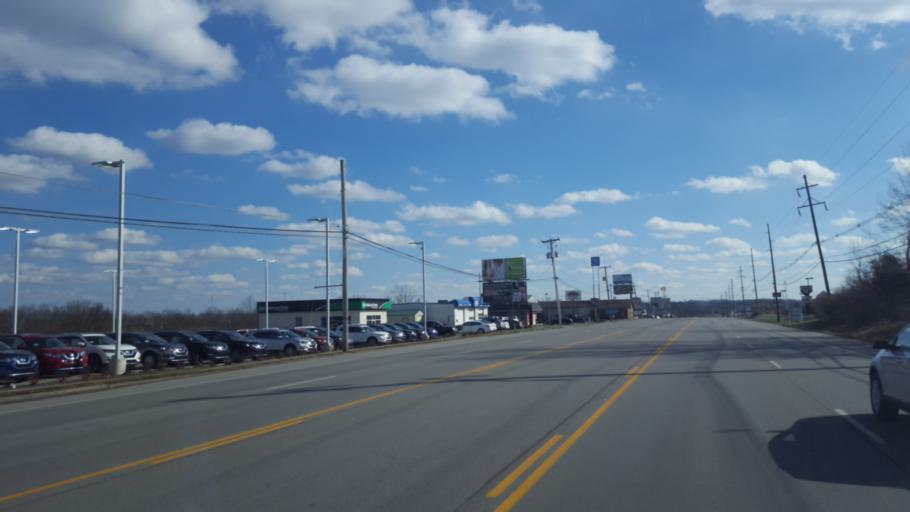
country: US
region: Kentucky
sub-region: Franklin County
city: Frankfort
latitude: 38.1828
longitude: -84.8173
